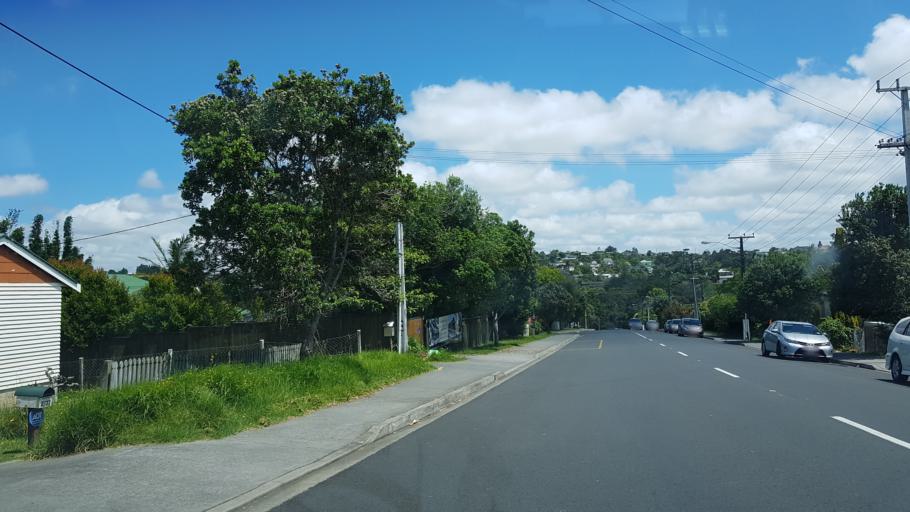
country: NZ
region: Auckland
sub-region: Auckland
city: North Shore
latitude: -36.7812
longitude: 174.7193
